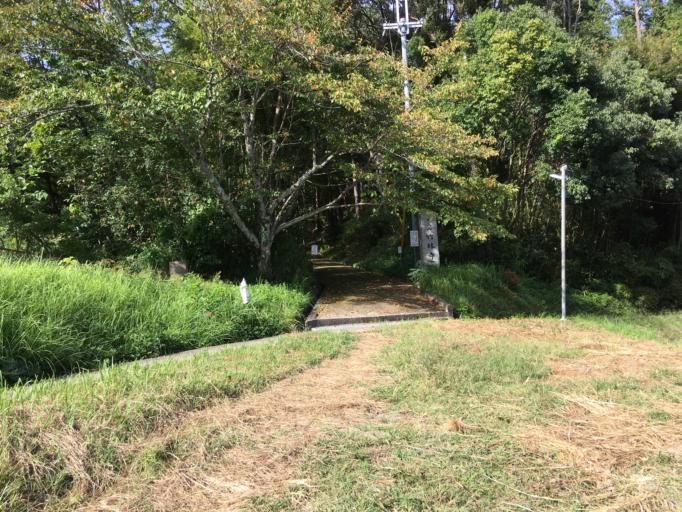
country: JP
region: Nara
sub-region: Ikoma-shi
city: Ikoma
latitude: 34.6714
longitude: 135.7037
